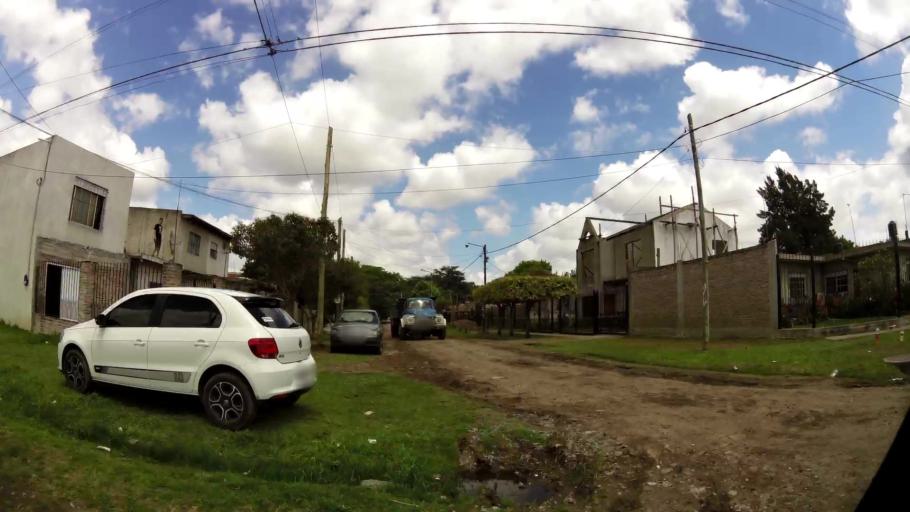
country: AR
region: Buenos Aires
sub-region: Partido de Quilmes
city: Quilmes
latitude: -34.8241
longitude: -58.2464
